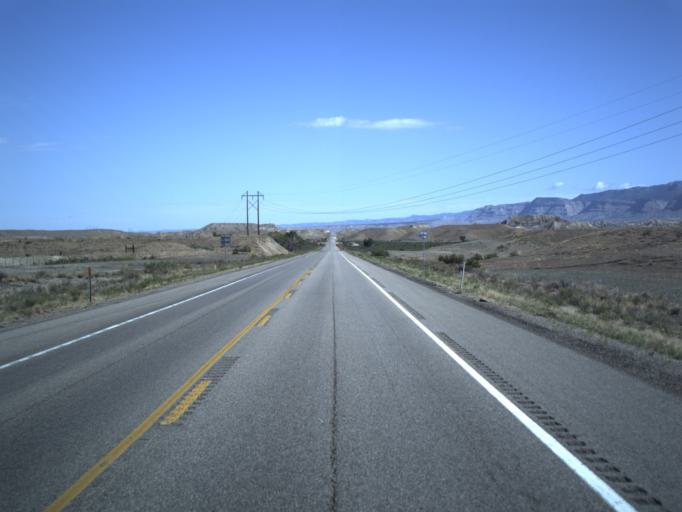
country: US
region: Utah
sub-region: Carbon County
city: East Carbon City
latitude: 39.2559
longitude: -110.3399
